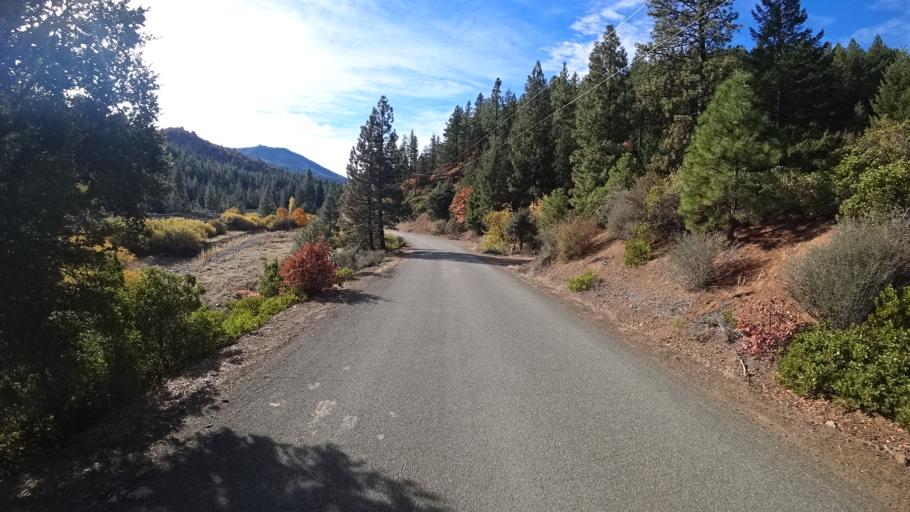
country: US
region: California
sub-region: Siskiyou County
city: Yreka
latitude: 41.7024
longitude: -122.8171
